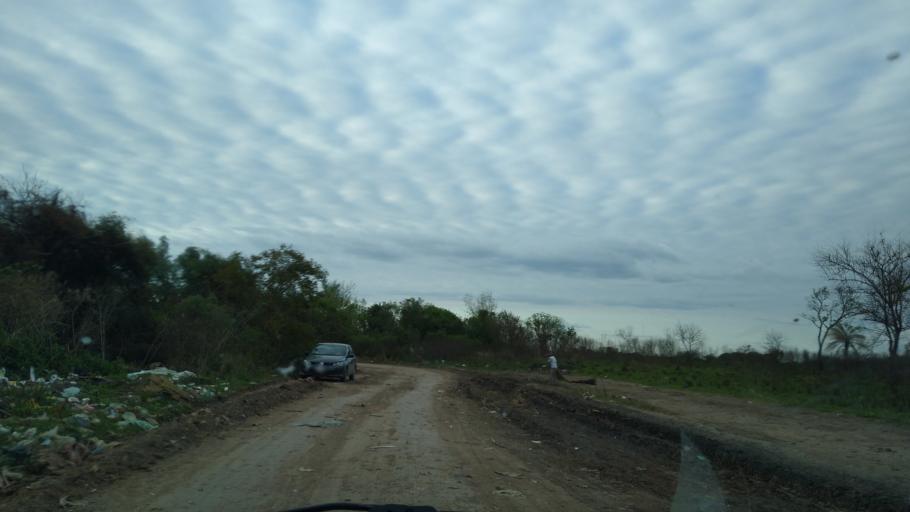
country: AR
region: Chaco
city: Fontana
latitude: -27.3941
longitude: -59.0496
